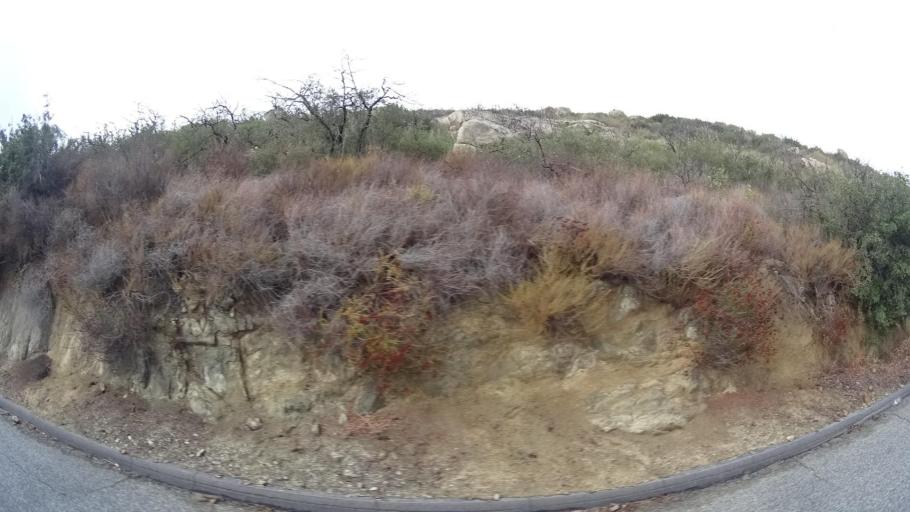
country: MX
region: Baja California
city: Tecate
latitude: 32.6024
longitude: -116.6037
